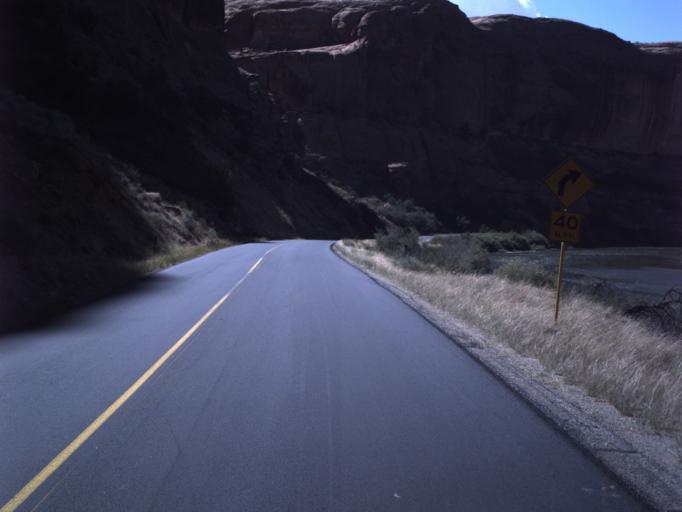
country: US
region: Utah
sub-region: Grand County
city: Moab
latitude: 38.6092
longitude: -109.5362
